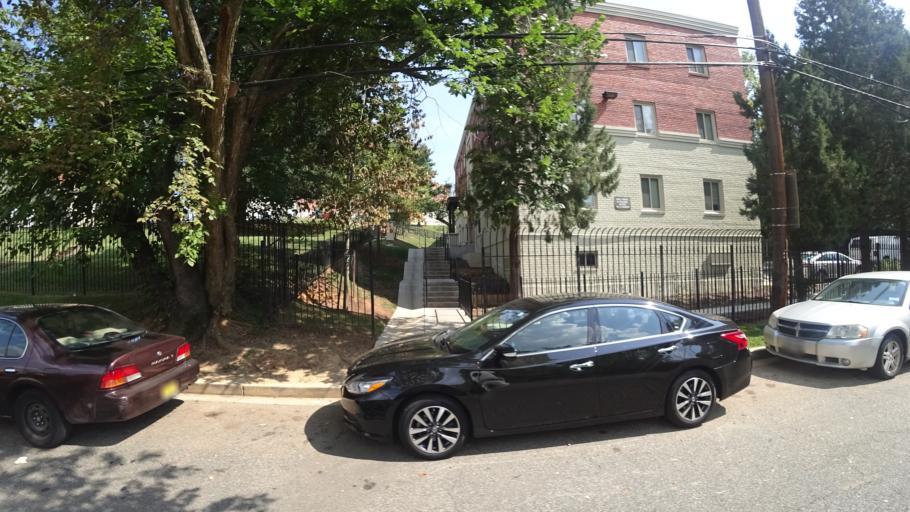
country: US
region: Maryland
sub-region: Prince George's County
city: Glassmanor
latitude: 38.8583
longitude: -76.9979
